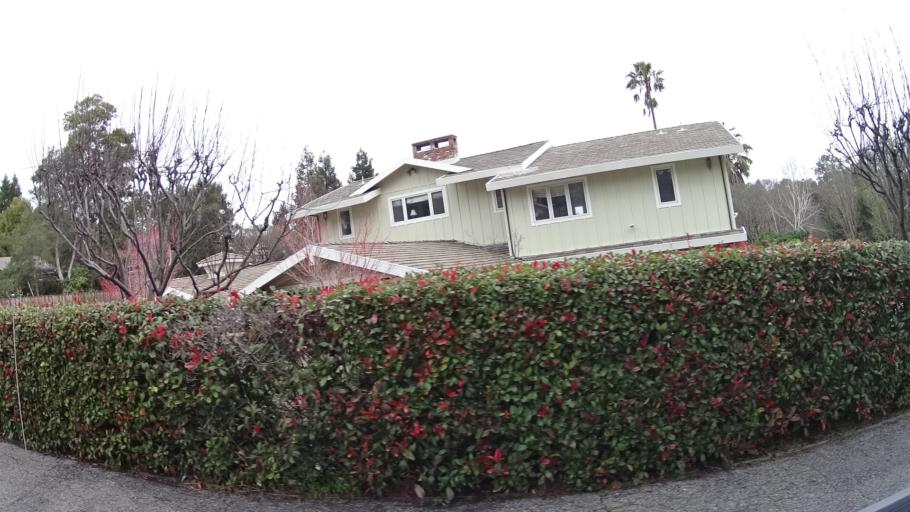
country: US
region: California
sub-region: San Mateo County
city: Hillsborough
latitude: 37.5510
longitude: -122.3716
